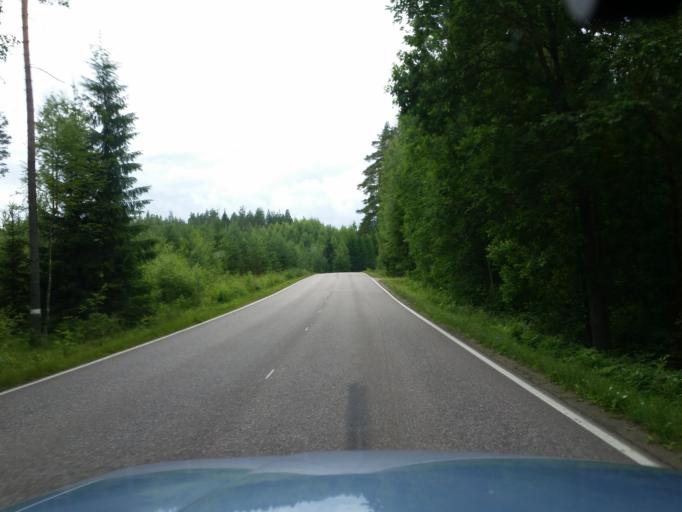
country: FI
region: Southern Savonia
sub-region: Savonlinna
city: Sulkava
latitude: 61.7958
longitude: 28.4093
